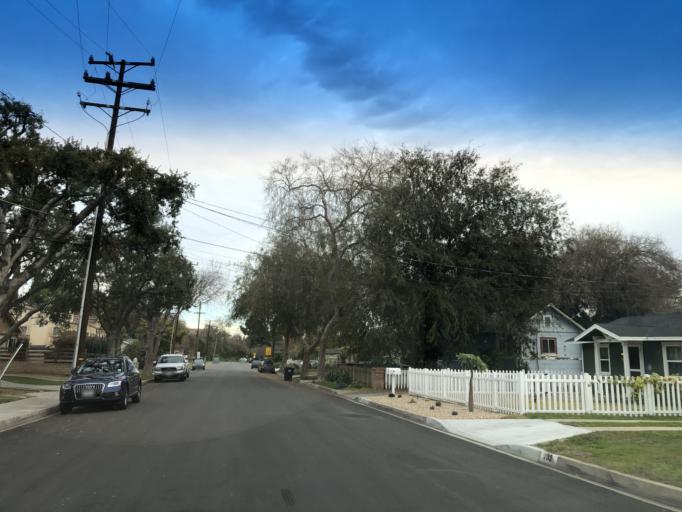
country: US
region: California
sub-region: Los Angeles County
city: Arcadia
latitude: 34.1370
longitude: -118.0156
